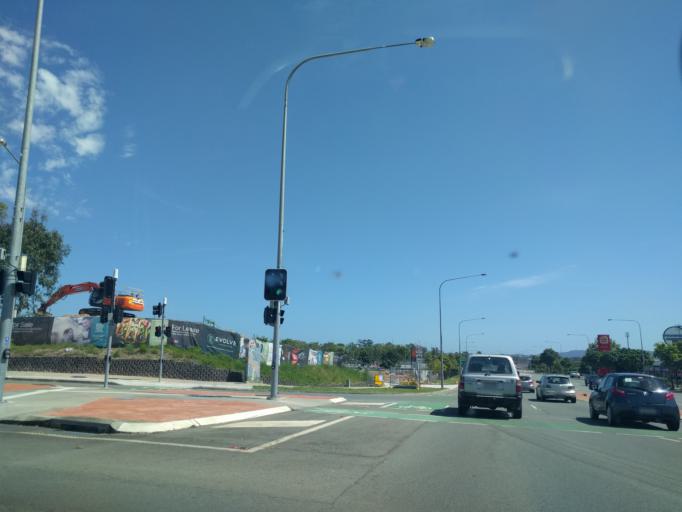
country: AU
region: Queensland
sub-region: Brisbane
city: Richlands
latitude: -27.5973
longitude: 152.9492
